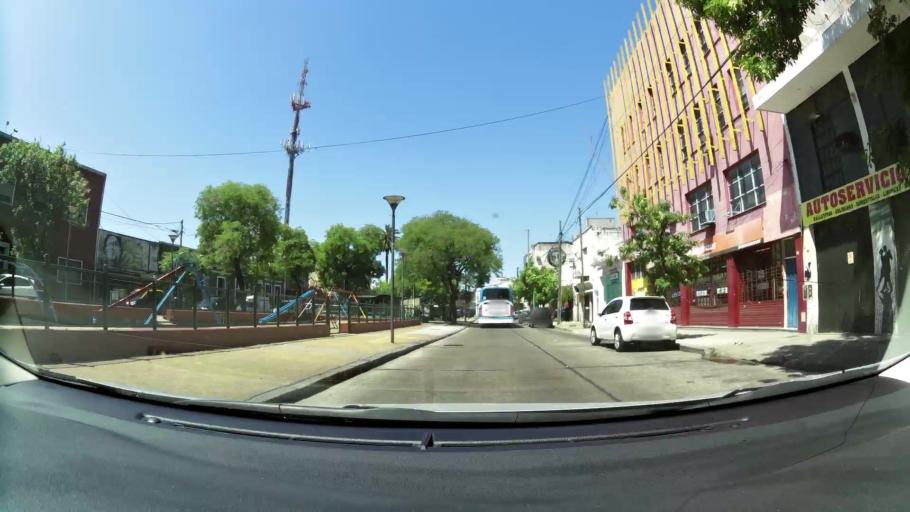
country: AR
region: Buenos Aires
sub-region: Partido de Avellaneda
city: Avellaneda
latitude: -34.6520
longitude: -58.4152
